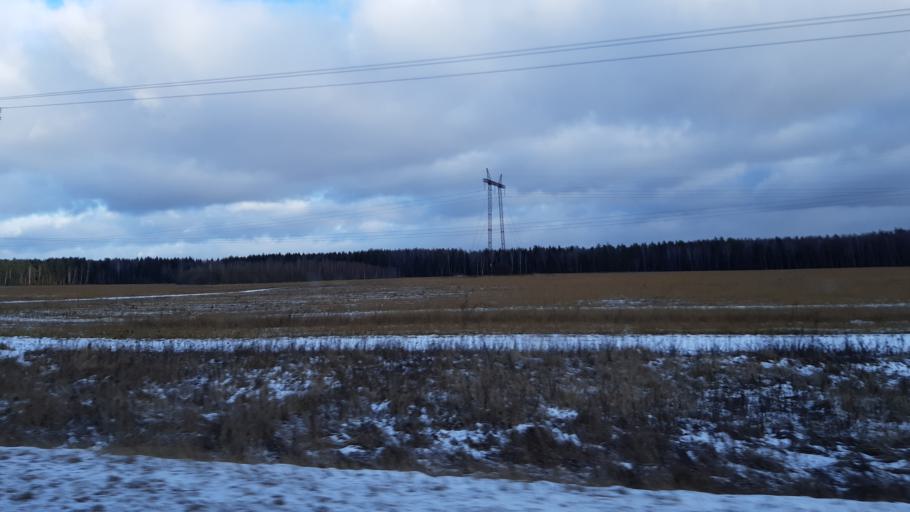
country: RU
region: Moskovskaya
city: Noginsk-9
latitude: 56.0398
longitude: 38.5532
